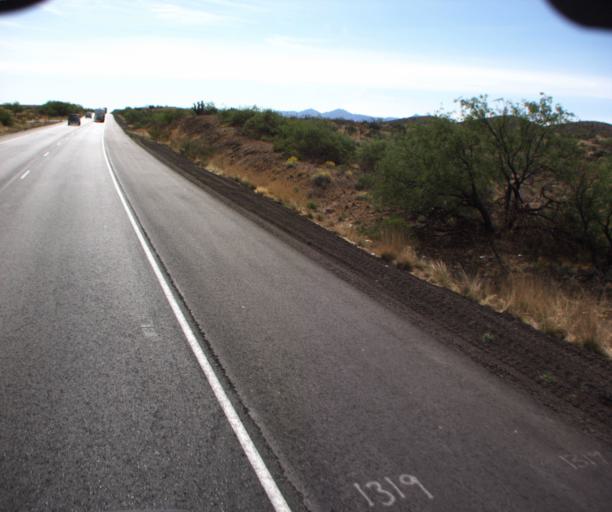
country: US
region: Arizona
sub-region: Pima County
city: Vail
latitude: 31.9978
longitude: -110.6249
